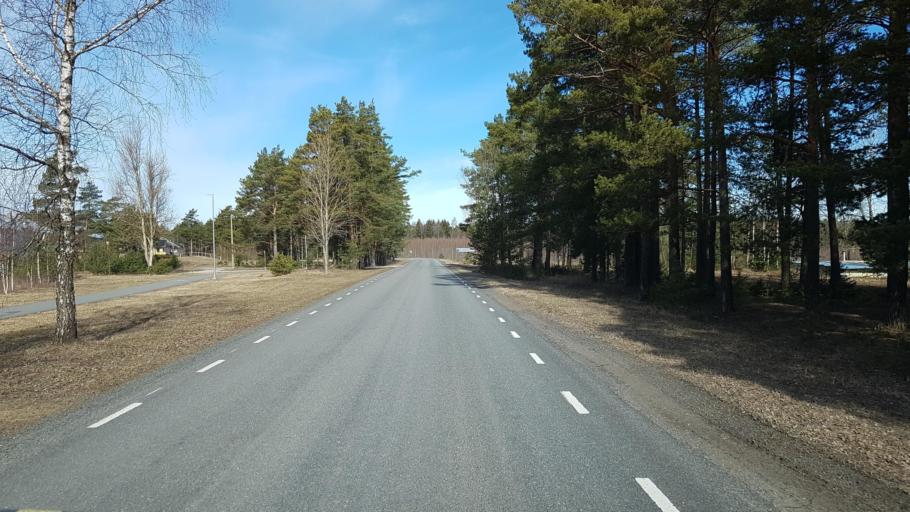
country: EE
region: Harju
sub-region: Nissi vald
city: Riisipere
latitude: 59.2472
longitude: 24.2417
